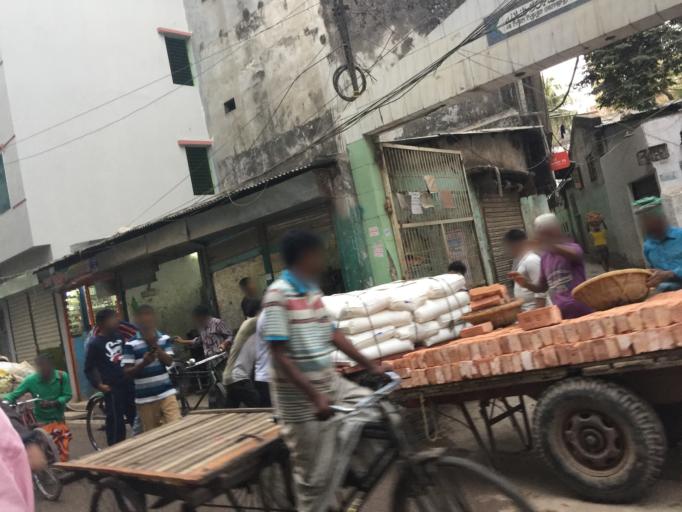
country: BD
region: Dhaka
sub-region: Dhaka
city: Dhaka
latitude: 23.7176
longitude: 90.4013
